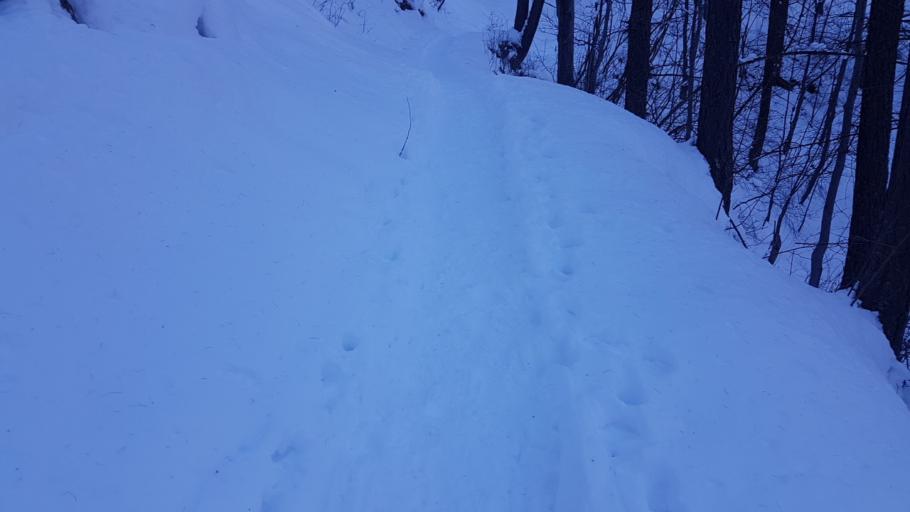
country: IT
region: Piedmont
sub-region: Provincia di Torino
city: Cesana Torinese
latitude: 44.9805
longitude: 6.8128
